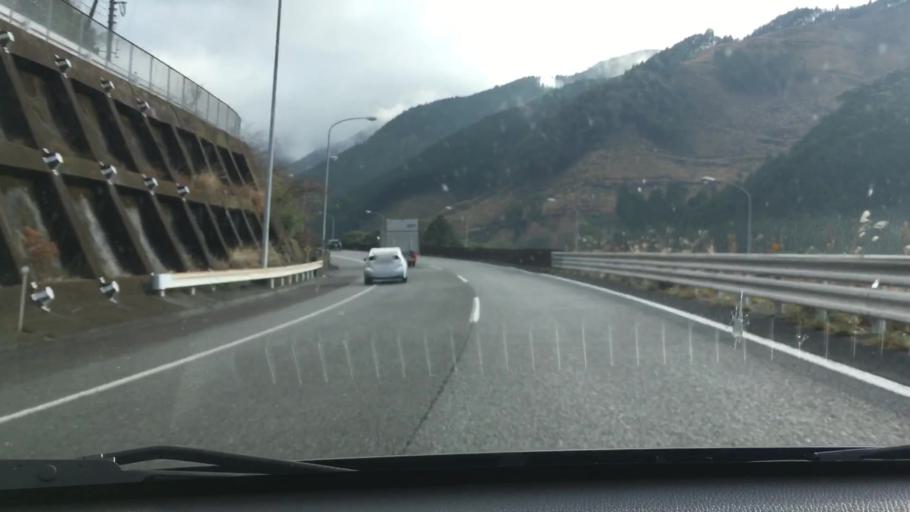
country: JP
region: Kumamoto
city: Yatsushiro
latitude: 32.4030
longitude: 130.6978
